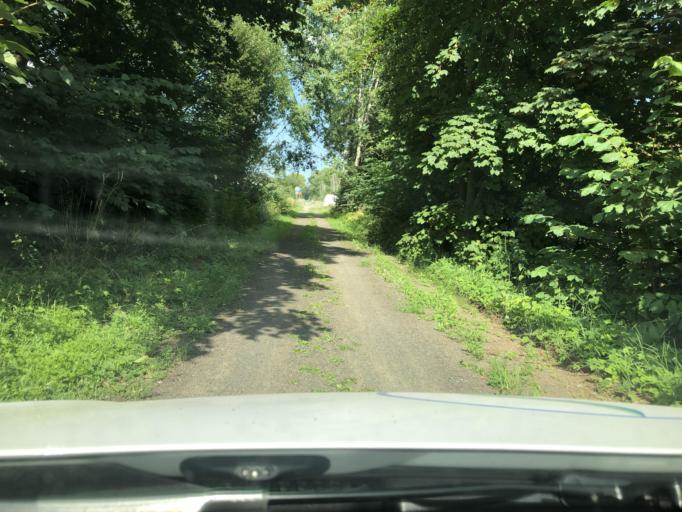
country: SE
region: Skane
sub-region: Kristianstads Kommun
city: Degeberga
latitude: 55.7703
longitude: 14.1556
